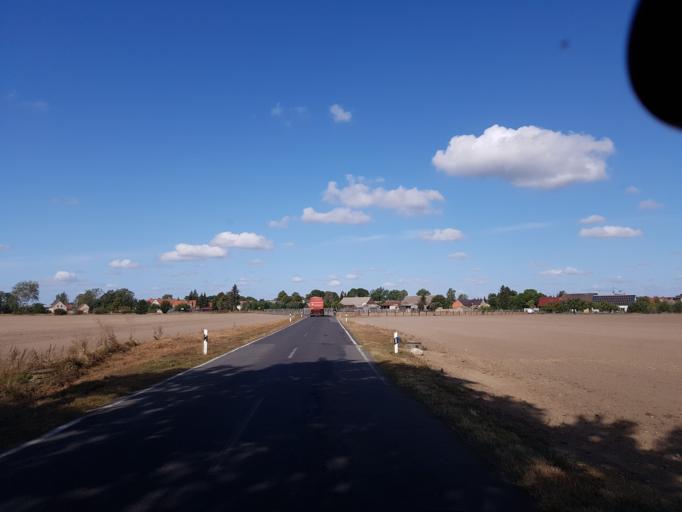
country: DE
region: Brandenburg
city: Sonnewalde
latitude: 51.7089
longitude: 13.6387
